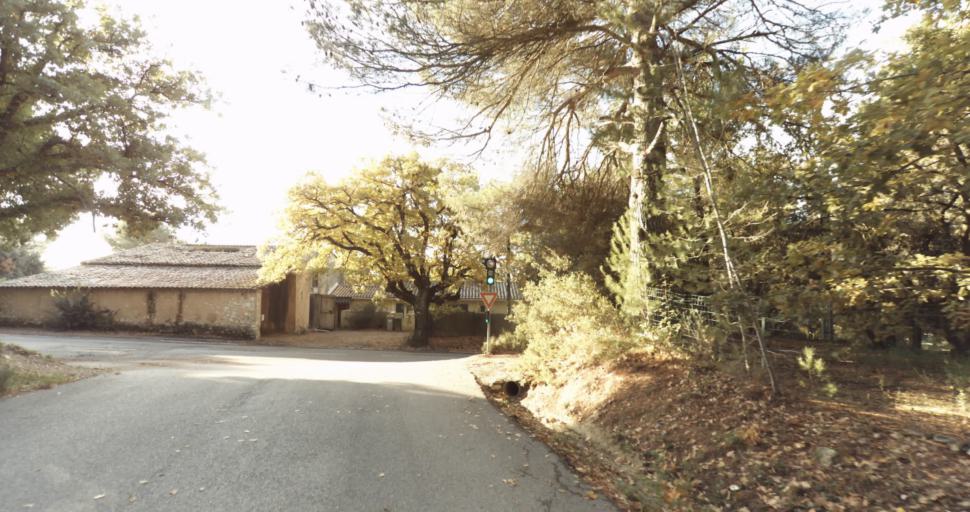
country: FR
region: Provence-Alpes-Cote d'Azur
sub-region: Departement des Bouches-du-Rhone
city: Venelles
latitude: 43.6009
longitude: 5.4745
